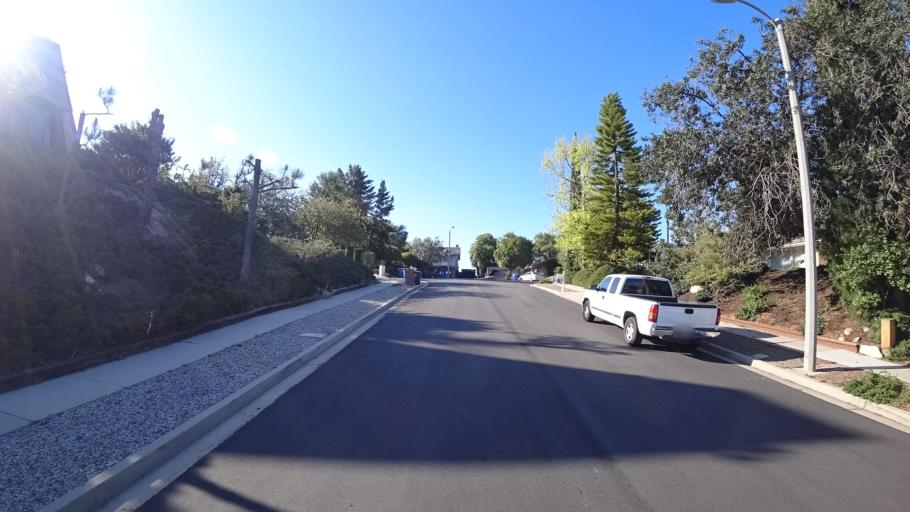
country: US
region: California
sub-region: Ventura County
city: Thousand Oaks
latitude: 34.1925
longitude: -118.8386
